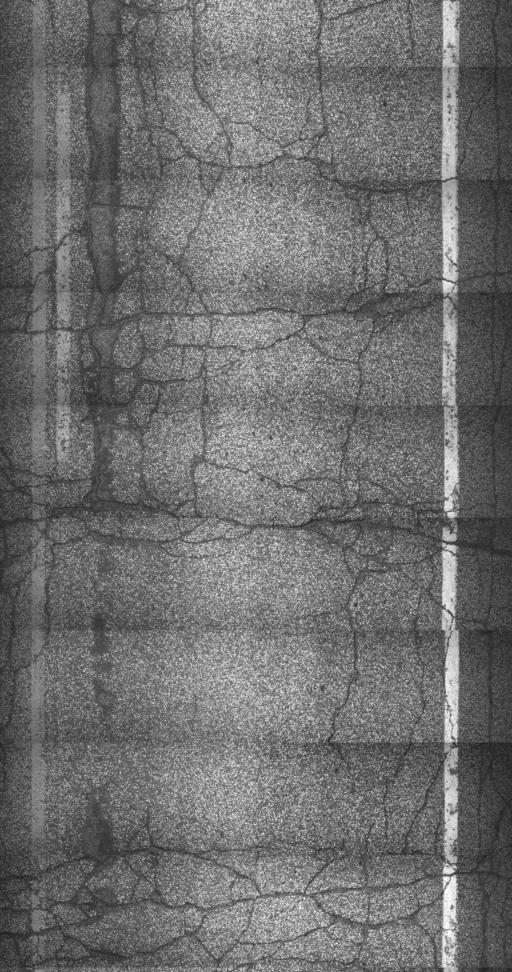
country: US
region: Vermont
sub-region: Orange County
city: Williamstown
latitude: 44.0328
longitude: -72.5909
